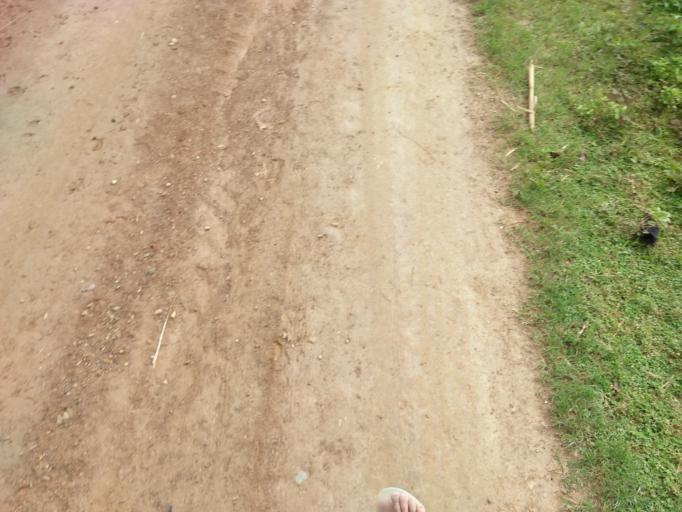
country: TH
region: Chiang Rai
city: Wiang Kaen
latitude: 19.8393
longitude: 100.7161
